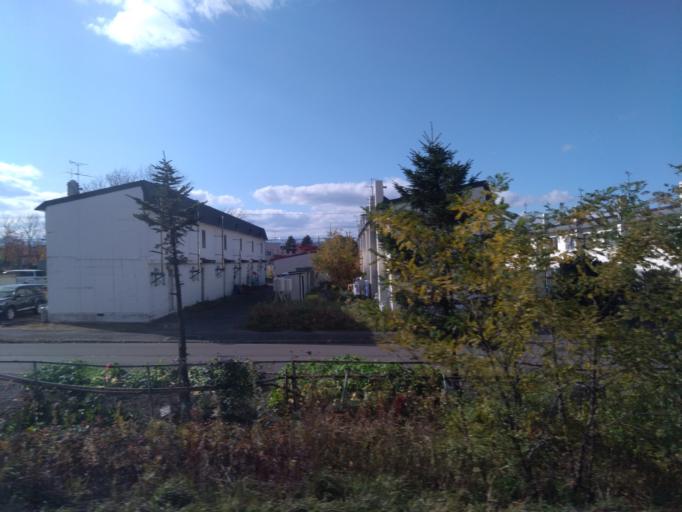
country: JP
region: Hokkaido
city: Kitahiroshima
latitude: 42.8974
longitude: 141.5748
